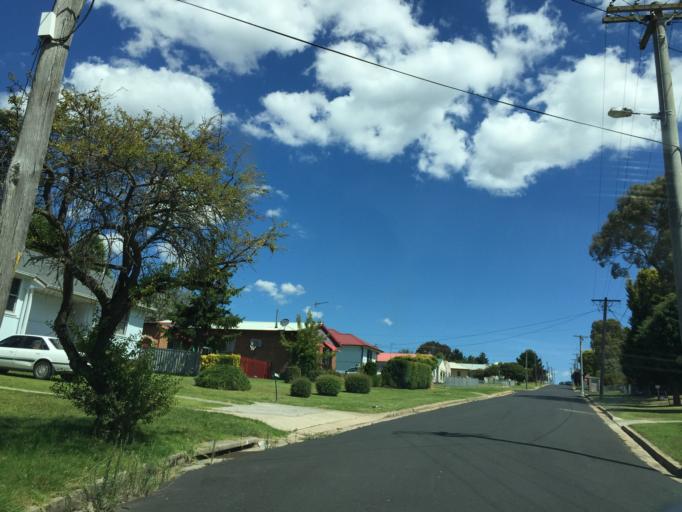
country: AU
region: New South Wales
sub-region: Lithgow
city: Lithgow
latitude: -33.4139
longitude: 150.0658
